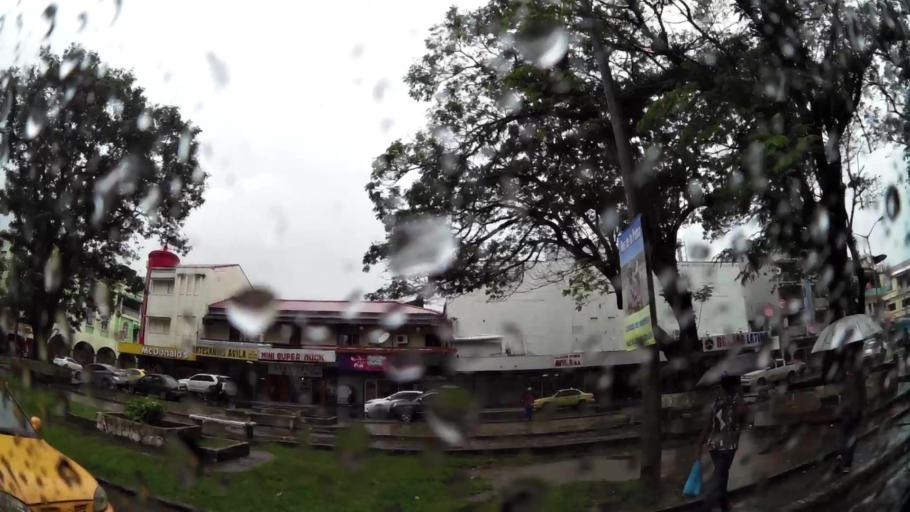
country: PA
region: Colon
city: Colon
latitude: 9.3581
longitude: -79.9017
